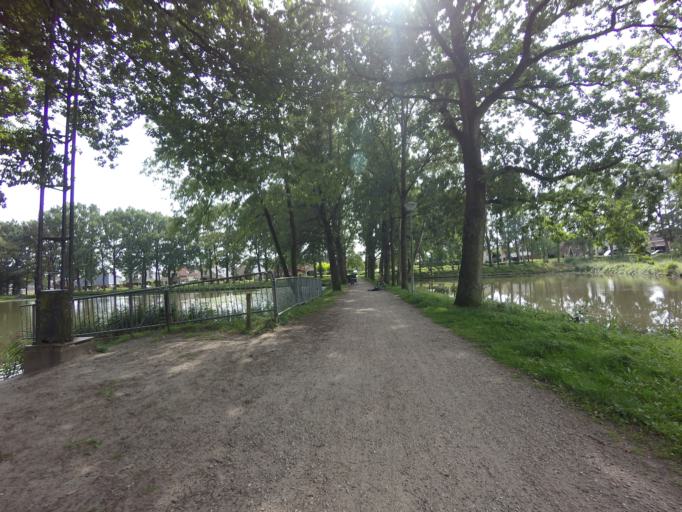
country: DE
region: Lower Saxony
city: Getelo
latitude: 52.4047
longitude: 6.9022
